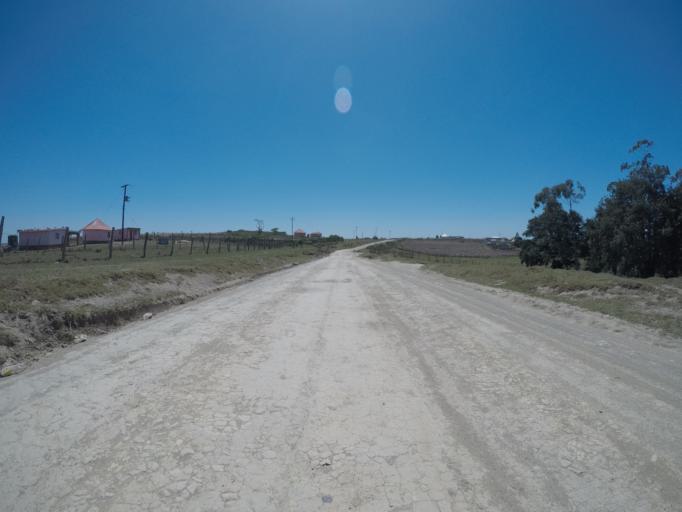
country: ZA
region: Eastern Cape
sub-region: OR Tambo District Municipality
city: Libode
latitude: -31.9481
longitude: 29.0252
